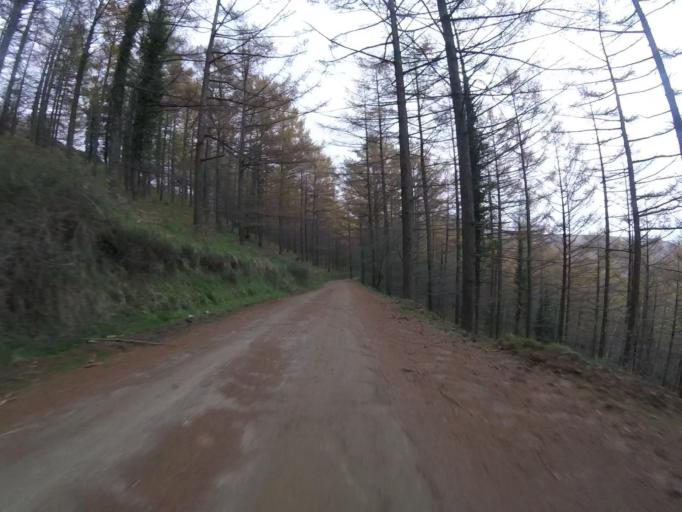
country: ES
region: Navarre
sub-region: Provincia de Navarra
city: Goizueta
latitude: 43.1831
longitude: -1.8133
